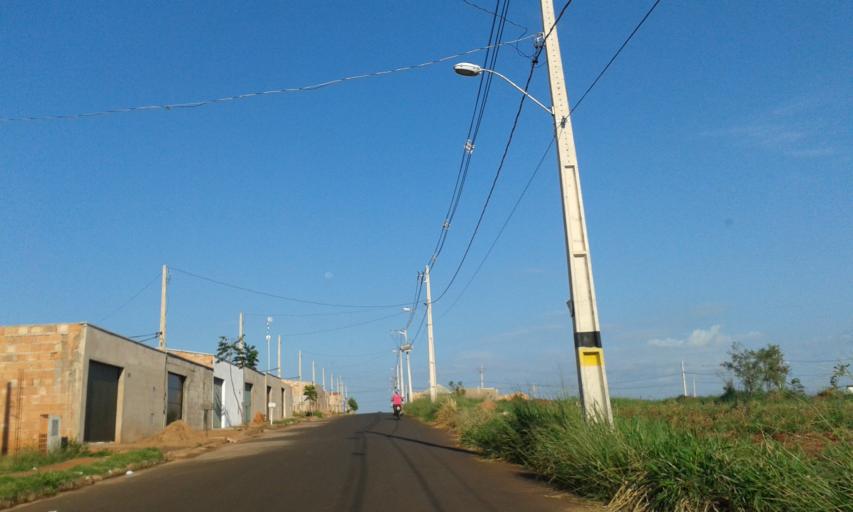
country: BR
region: Minas Gerais
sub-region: Ituiutaba
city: Ituiutaba
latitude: -19.0155
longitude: -49.4560
